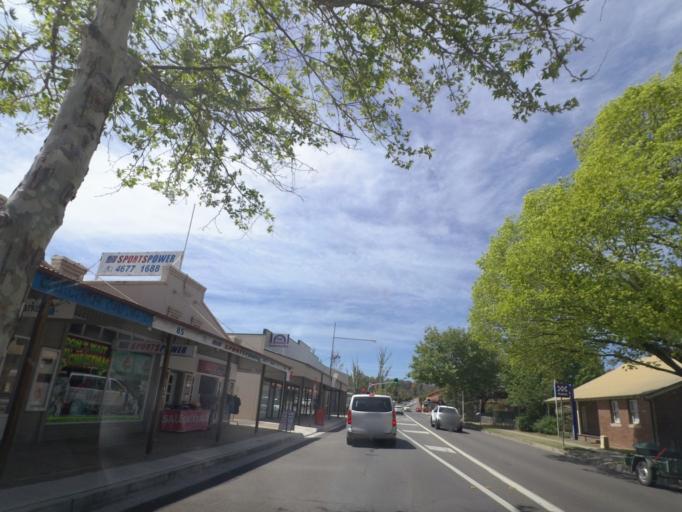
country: AU
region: New South Wales
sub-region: Wollondilly
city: Picton
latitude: -34.1682
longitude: 150.6119
